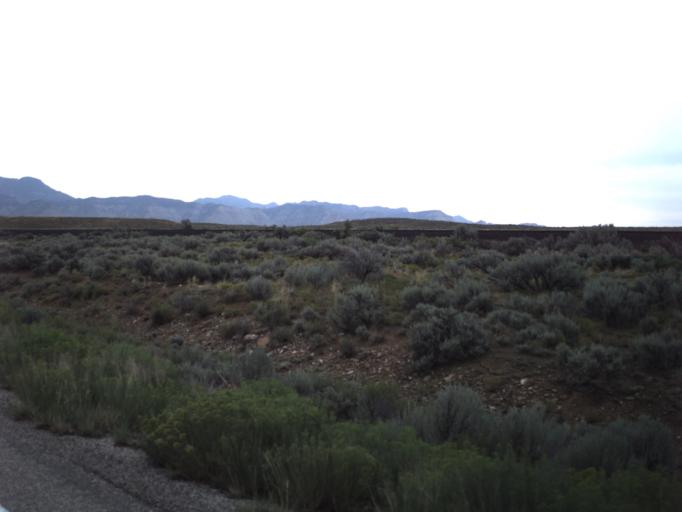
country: US
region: Utah
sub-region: Carbon County
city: East Carbon City
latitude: 39.5342
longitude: -110.5211
